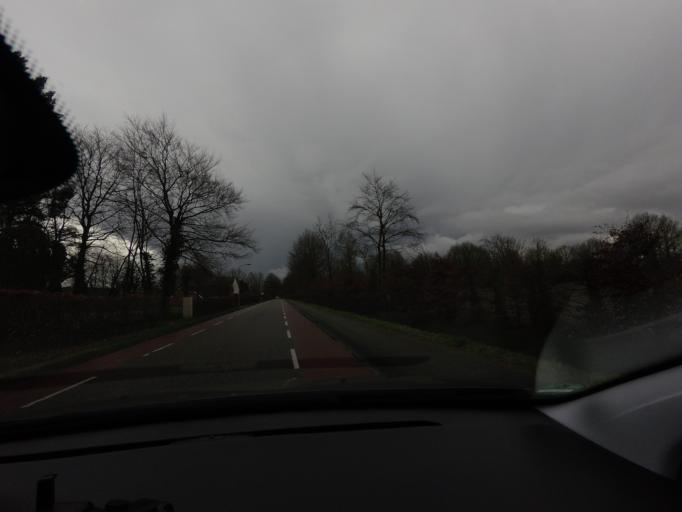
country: NL
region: Drenthe
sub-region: Gemeente Borger-Odoorn
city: Borger
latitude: 52.9894
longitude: 6.7774
